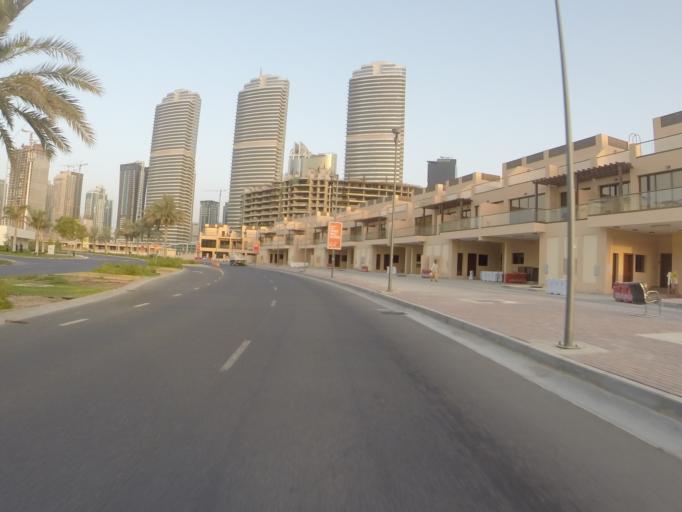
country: AE
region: Dubai
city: Dubai
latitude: 25.0676
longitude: 55.1495
